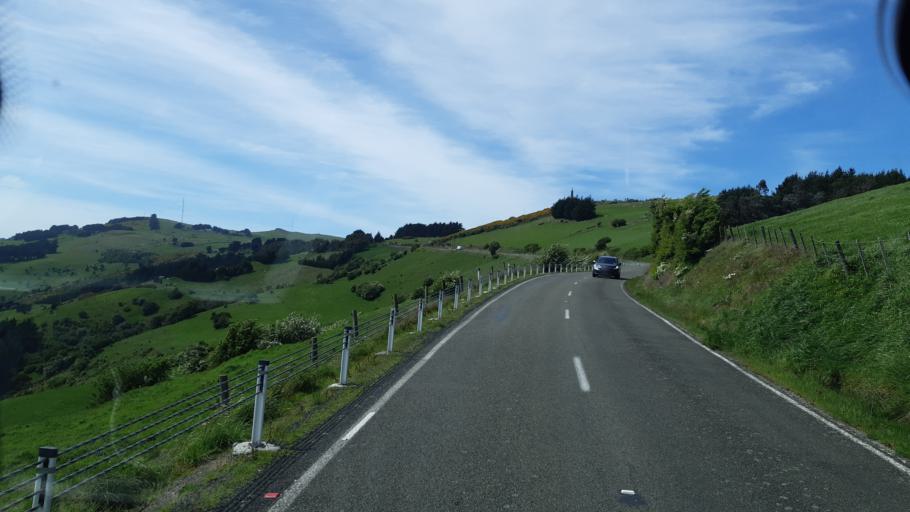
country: NZ
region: Otago
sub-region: Dunedin City
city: Dunedin
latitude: -45.8834
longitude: 170.5584
